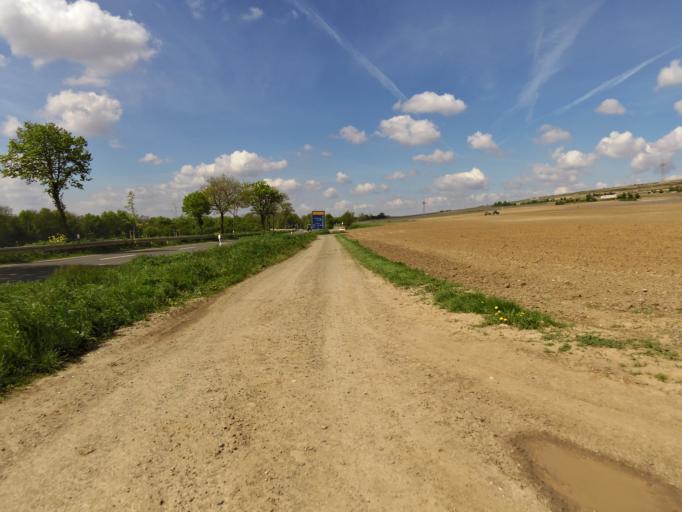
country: DE
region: Rheinland-Pfalz
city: Gundersheim
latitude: 49.7018
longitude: 8.2137
